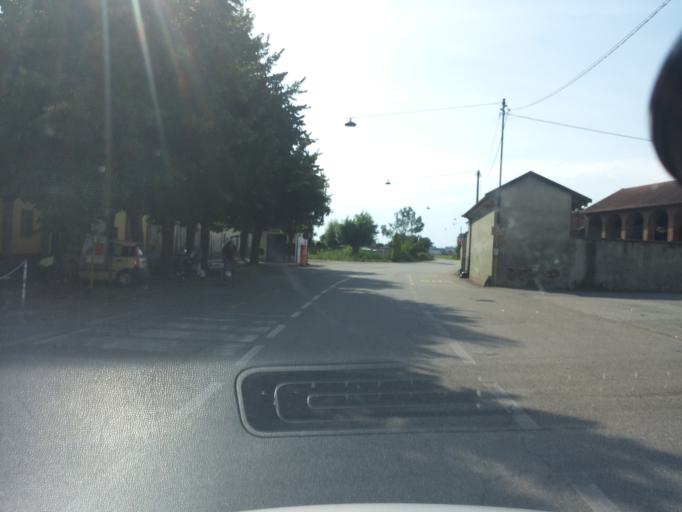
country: IT
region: Piedmont
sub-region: Provincia di Vercelli
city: Crova
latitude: 45.3263
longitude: 8.2314
